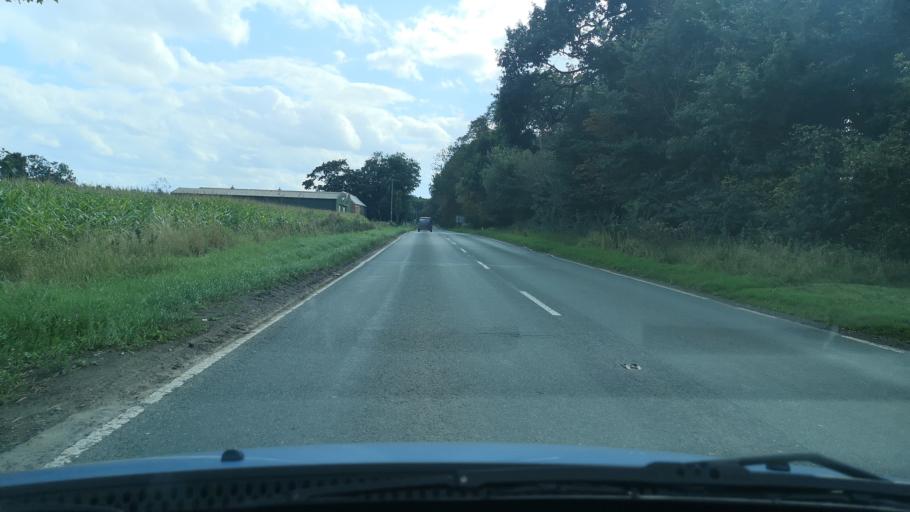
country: GB
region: England
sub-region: North Lincolnshire
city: Crowle
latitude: 53.5834
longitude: -0.8199
